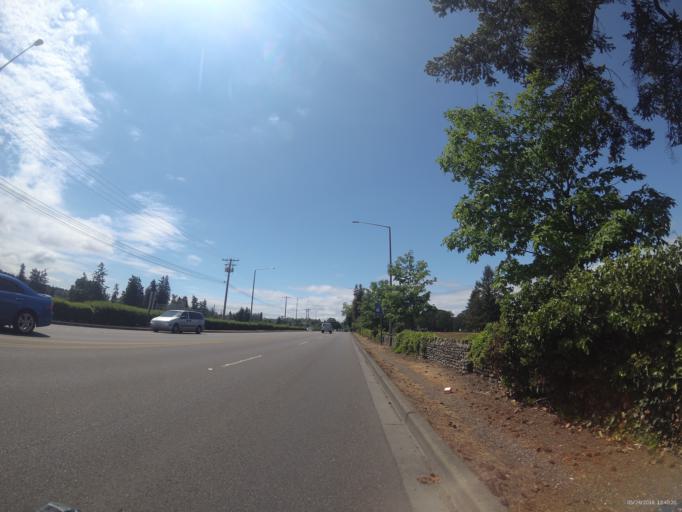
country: US
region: Washington
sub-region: Pierce County
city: Lakewood
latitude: 47.1791
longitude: -122.5548
